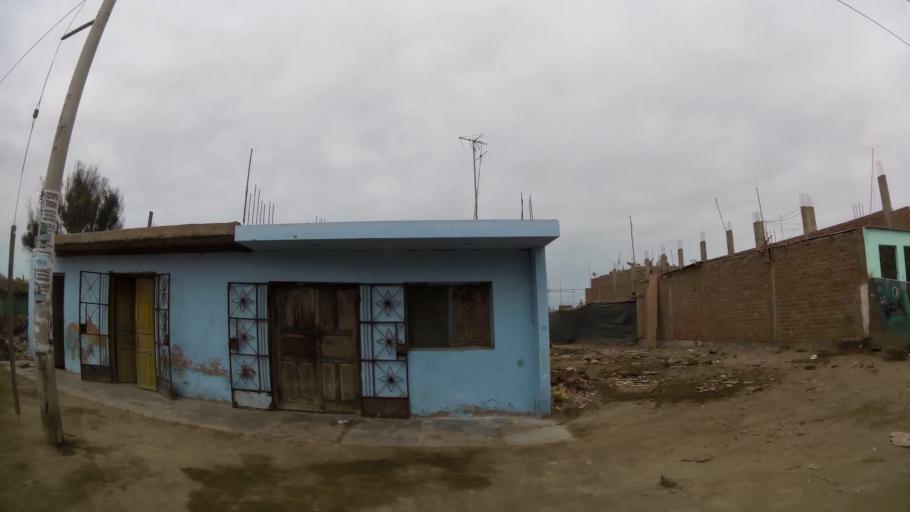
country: PE
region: Lima
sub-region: Provincia de Canete
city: Chilca
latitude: -12.5184
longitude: -76.7334
